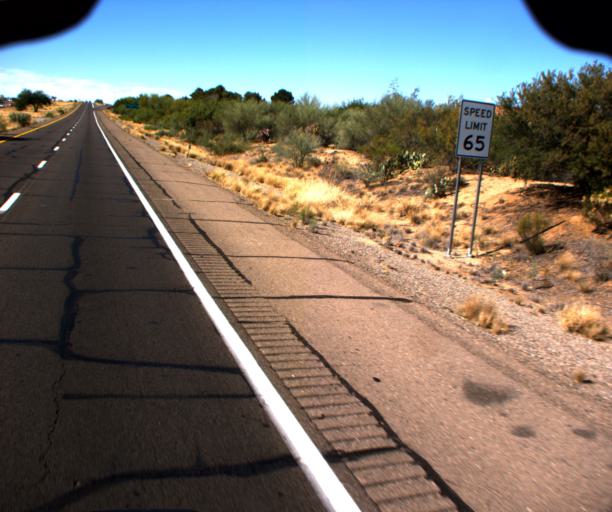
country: US
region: Arizona
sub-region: Pima County
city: Green Valley
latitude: 31.8591
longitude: -110.9925
